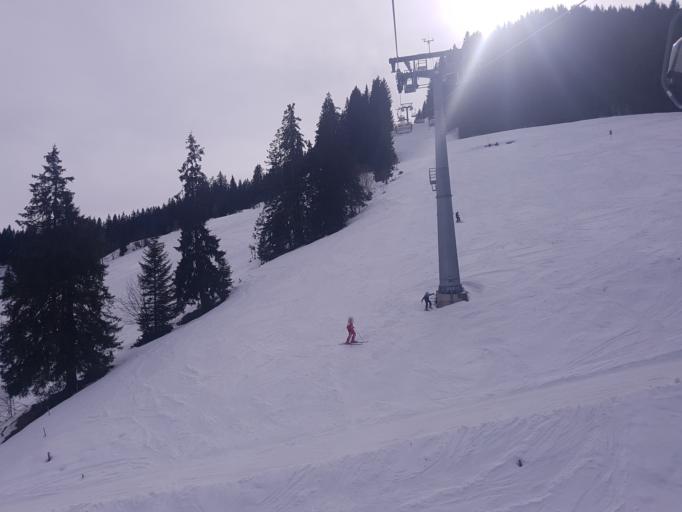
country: AT
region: Tyrol
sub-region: Politischer Bezirk Kufstein
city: Worgl
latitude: 47.4363
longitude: 12.0839
